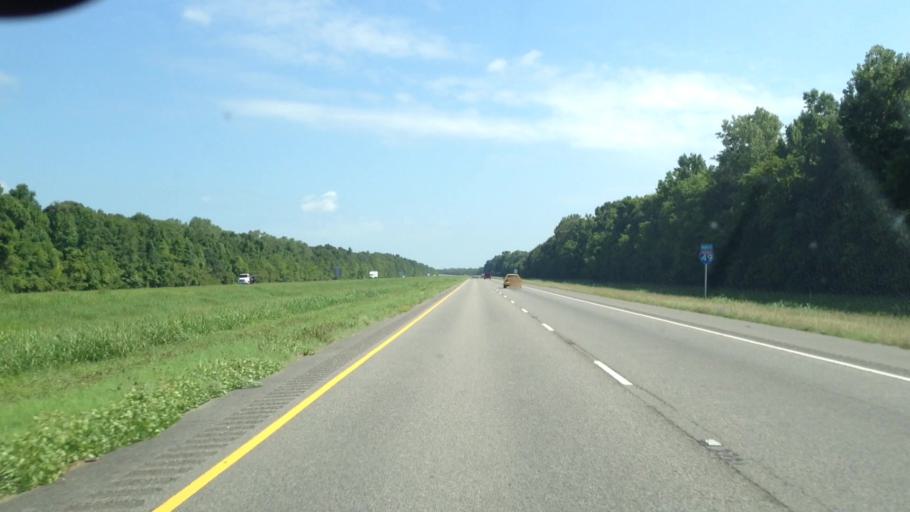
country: US
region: Louisiana
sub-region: Avoyelles Parish
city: Bunkie
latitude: 30.8745
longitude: -92.2273
